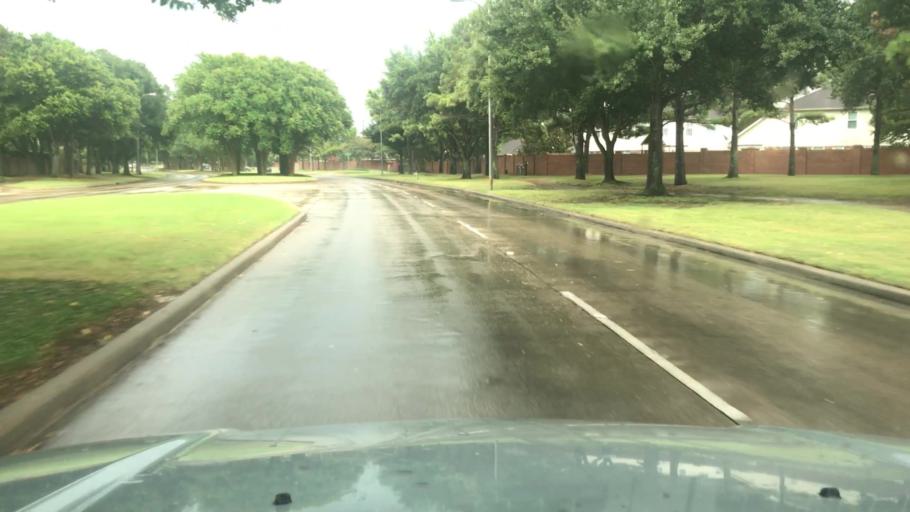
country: US
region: Texas
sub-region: Fort Bend County
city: Cinco Ranch
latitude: 29.7401
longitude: -95.7866
